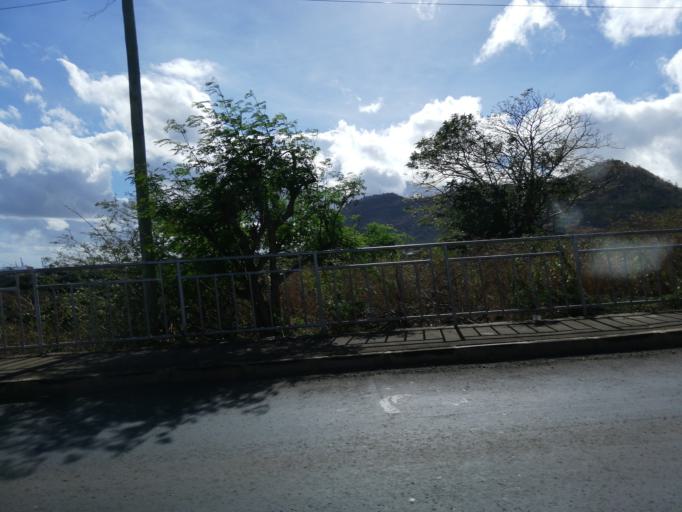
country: MU
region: Moka
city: Pailles
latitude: -20.1820
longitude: 57.4753
